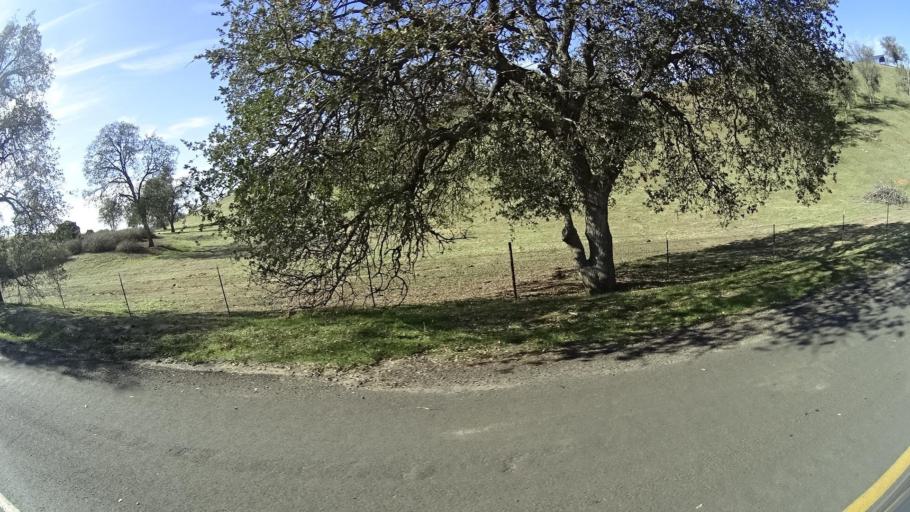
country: US
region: California
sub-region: Kern County
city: Oildale
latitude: 35.6470
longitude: -118.8403
